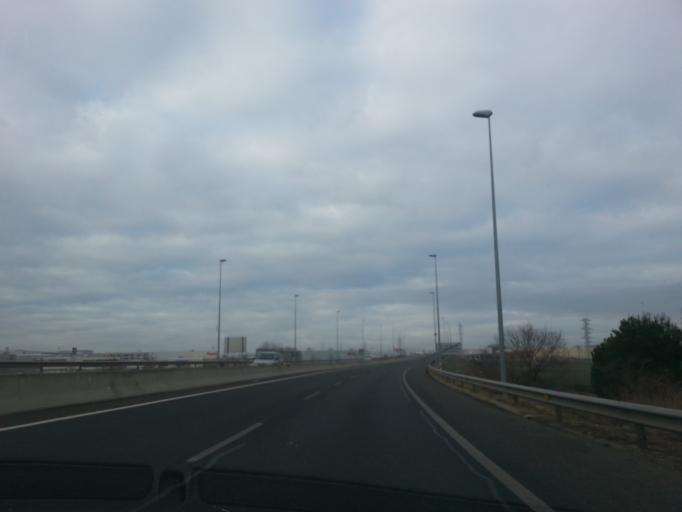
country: ES
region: Castille and Leon
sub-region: Provincia de Salamanca
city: Carbajosa de la Sagrada
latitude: 40.9419
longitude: -5.6465
